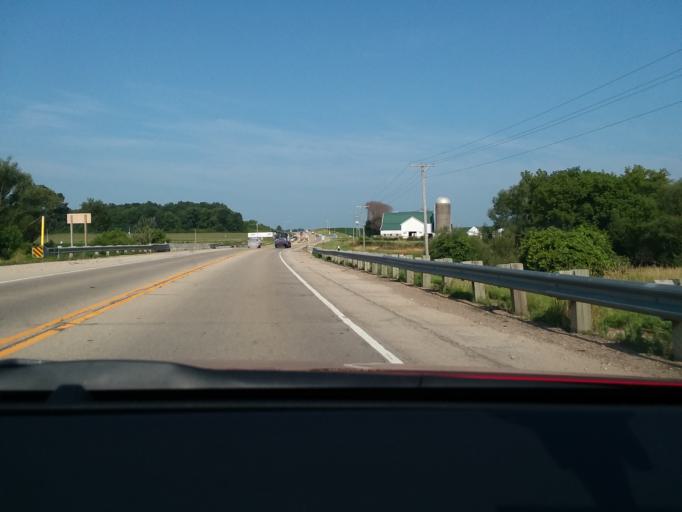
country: US
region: Wisconsin
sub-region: Dane County
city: Windsor
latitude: 43.1946
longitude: -89.3610
